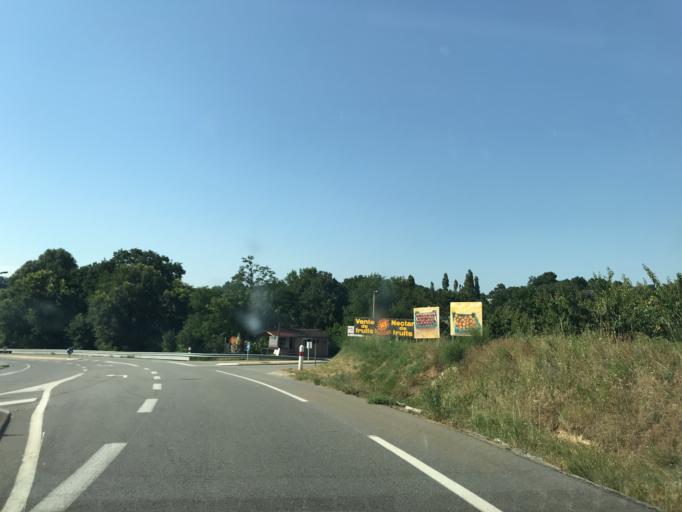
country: FR
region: Rhone-Alpes
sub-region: Departement de la Drome
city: Chateauneuf-sur-Isere
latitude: 45.0133
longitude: 4.9499
